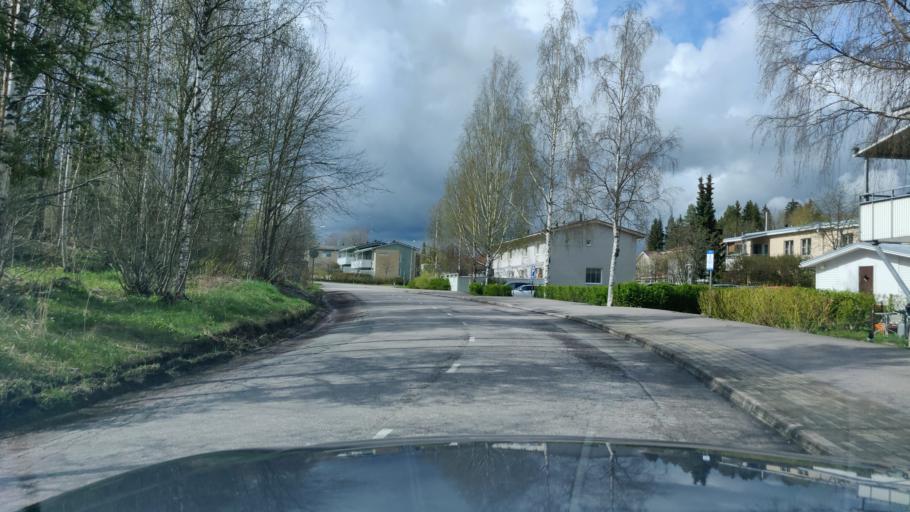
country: FI
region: Uusimaa
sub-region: Helsinki
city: Nurmijaervi
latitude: 60.3648
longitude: 24.7369
